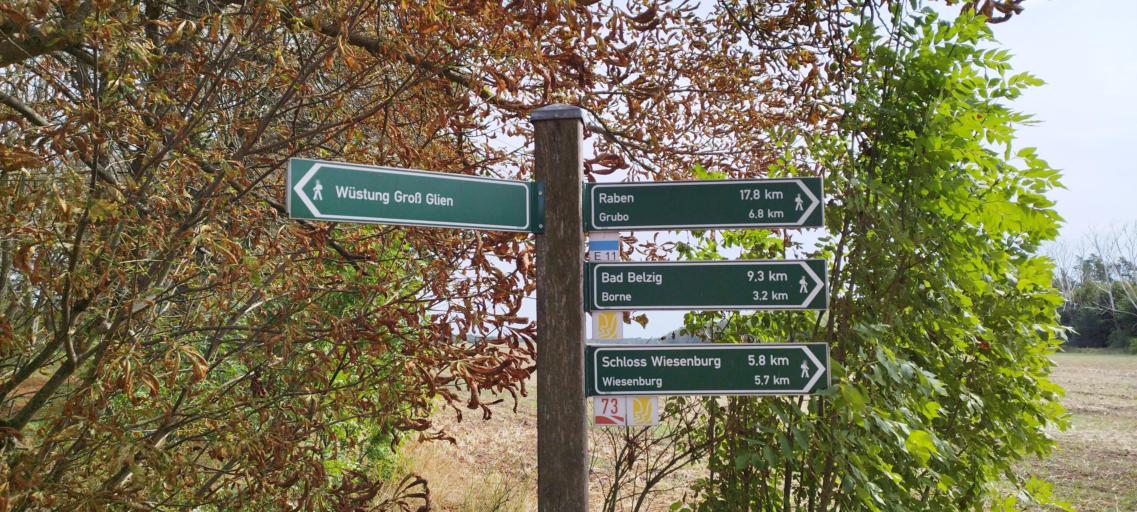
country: DE
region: Brandenburg
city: Wiesenburg
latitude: 52.1222
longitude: 12.5057
